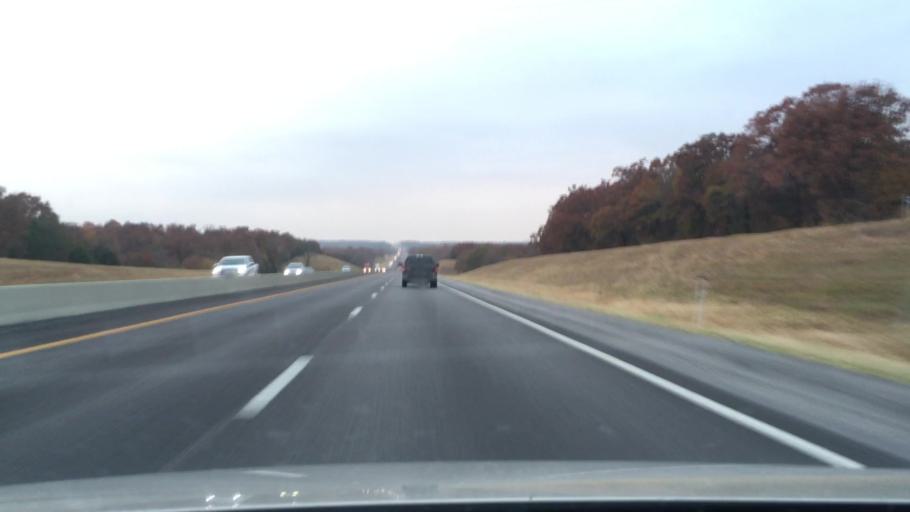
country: US
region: Oklahoma
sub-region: Lincoln County
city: Stroud
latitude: 35.7448
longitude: -96.7335
